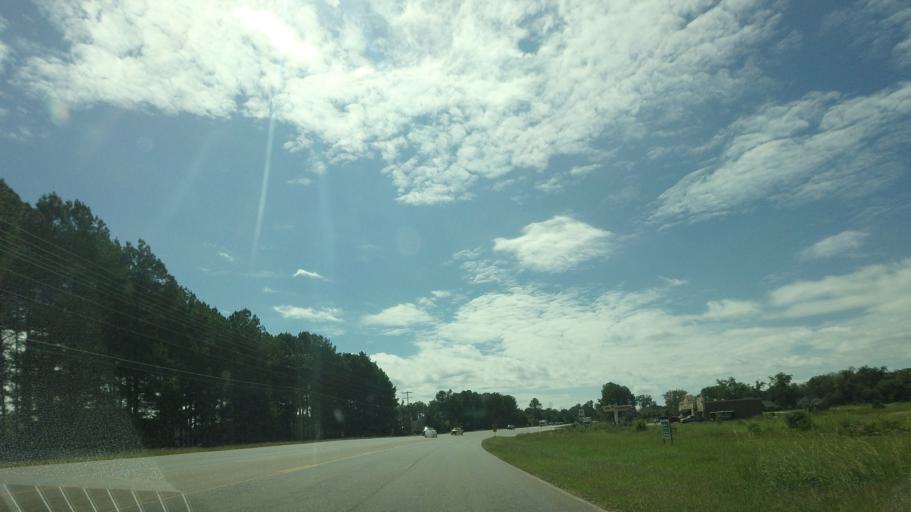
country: US
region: Georgia
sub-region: Houston County
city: Centerville
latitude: 32.5734
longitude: -83.6918
